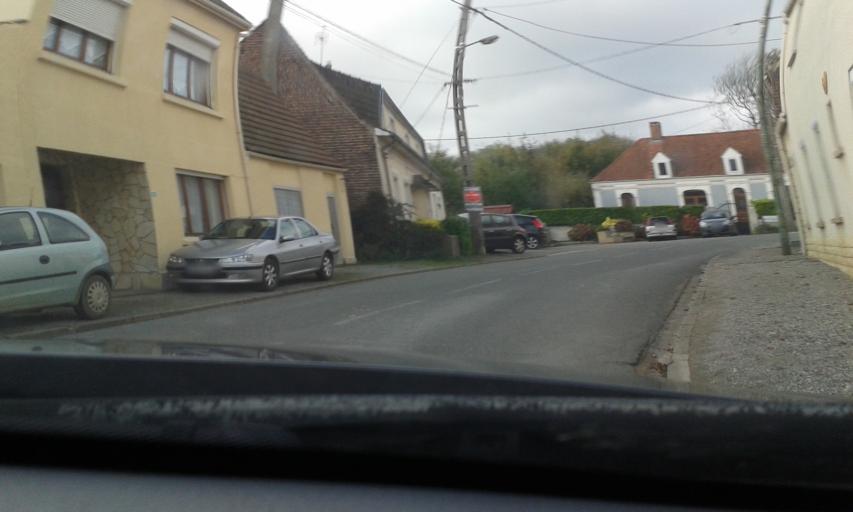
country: FR
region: Nord-Pas-de-Calais
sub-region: Departement du Pas-de-Calais
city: Ferques
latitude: 50.8720
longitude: 1.7864
